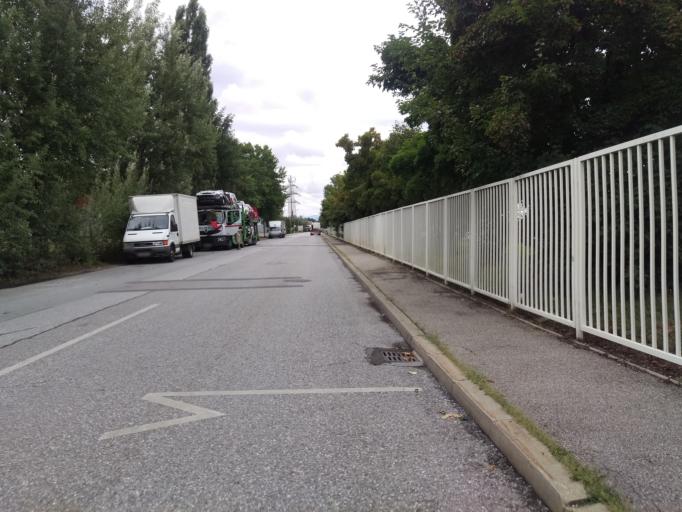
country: AT
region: Styria
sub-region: Politischer Bezirk Graz-Umgebung
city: Raaba
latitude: 47.0412
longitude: 15.4810
